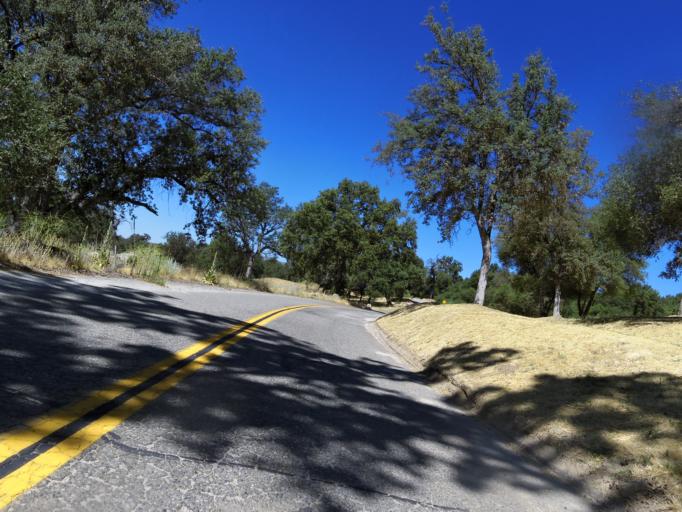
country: US
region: California
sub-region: Madera County
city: Ahwahnee
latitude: 37.3698
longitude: -119.7012
